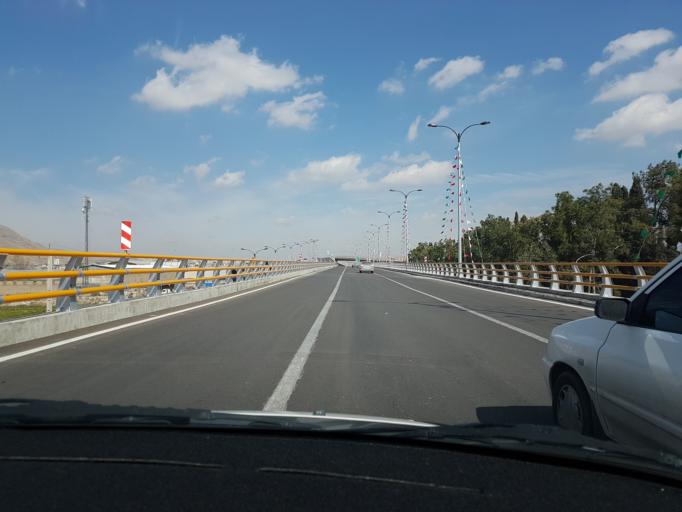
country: IR
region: Fars
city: Shiraz
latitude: 29.6128
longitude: 52.4681
